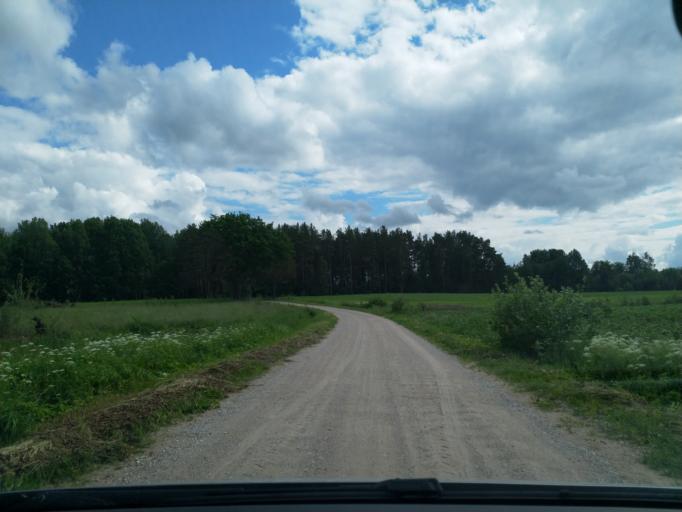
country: LV
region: Kuldigas Rajons
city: Kuldiga
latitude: 56.8400
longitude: 21.9513
